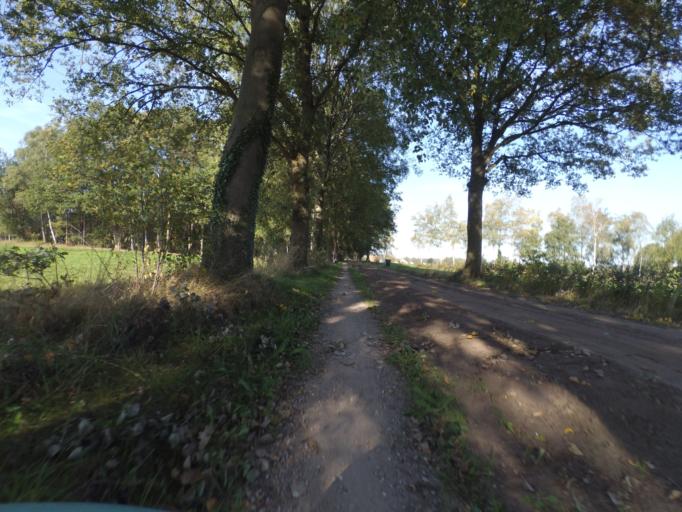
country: NL
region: Gelderland
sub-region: Gemeente Lochem
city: Barchem
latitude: 52.1072
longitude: 6.4181
